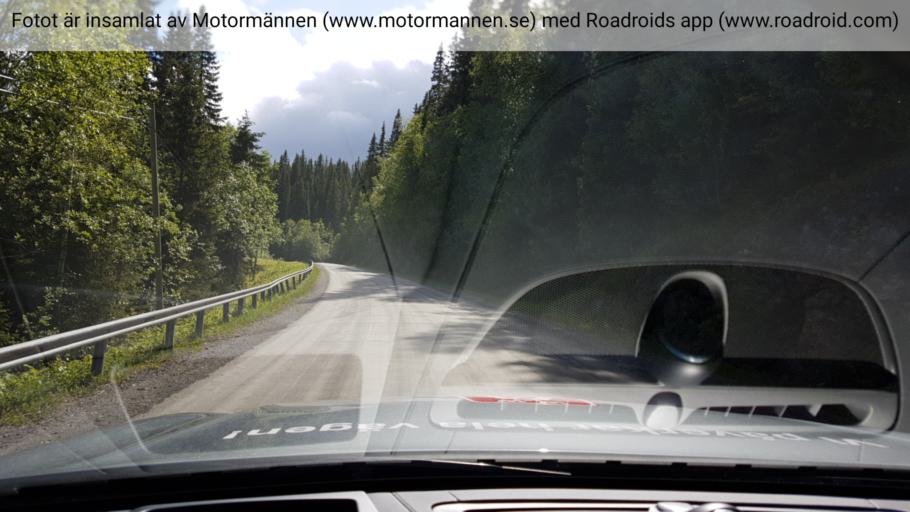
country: SE
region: Jaemtland
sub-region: Are Kommun
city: Are
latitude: 63.6930
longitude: 12.9302
